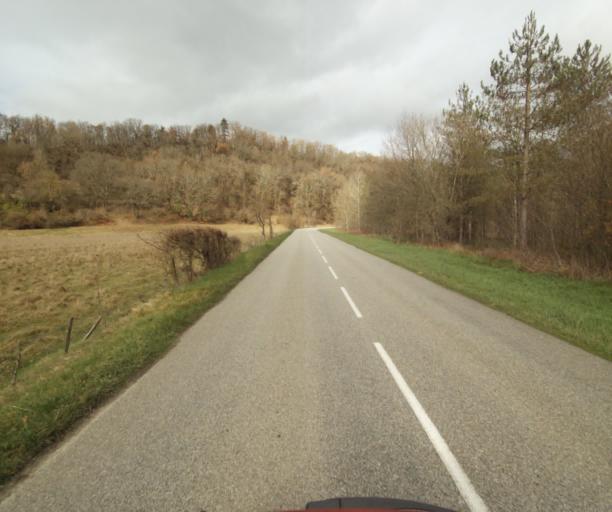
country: FR
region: Midi-Pyrenees
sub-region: Departement de l'Ariege
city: Pamiers
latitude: 43.1450
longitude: 1.5903
